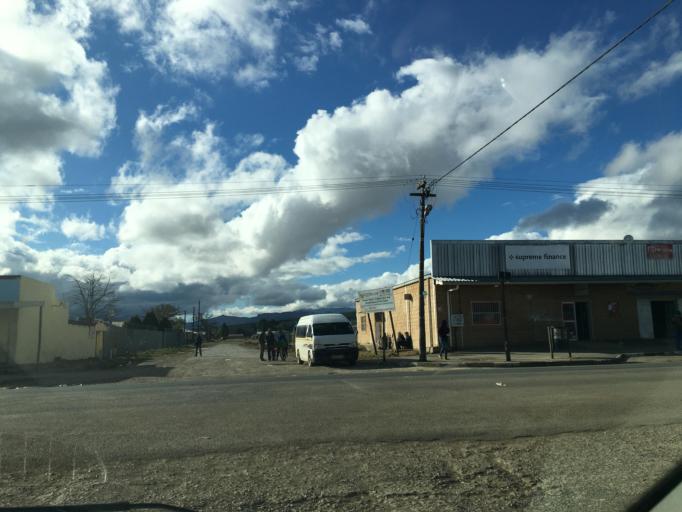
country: ZA
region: Eastern Cape
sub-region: Chris Hani District Municipality
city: Elliot
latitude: -31.3354
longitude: 27.8462
